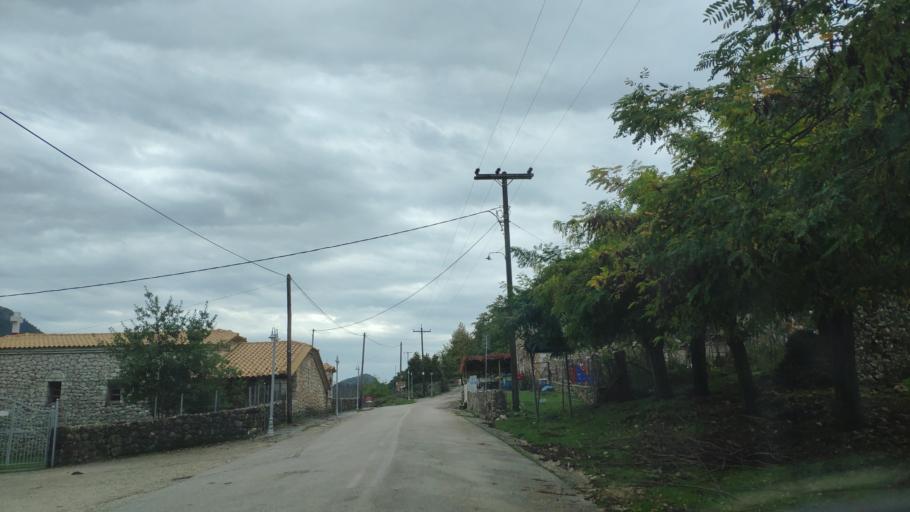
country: GR
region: Epirus
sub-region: Nomos Prevezis
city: Kanalaki
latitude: 39.3600
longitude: 20.6409
